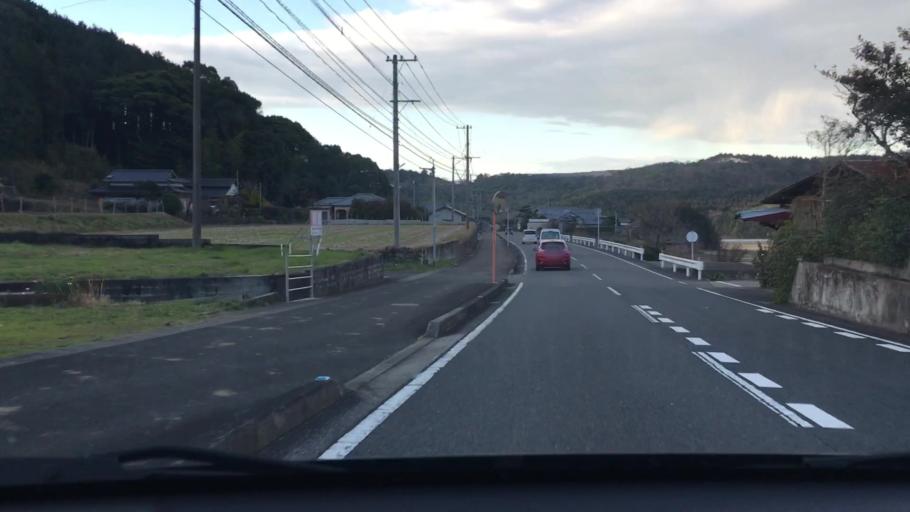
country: JP
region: Oita
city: Bungo-Takada-shi
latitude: 33.4976
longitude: 131.3768
